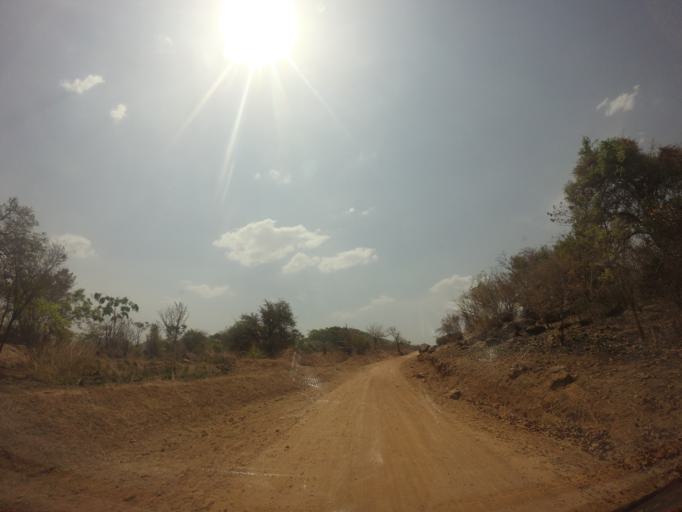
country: UG
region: Northern Region
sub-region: Arua District
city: Arua
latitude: 2.8976
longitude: 31.1110
